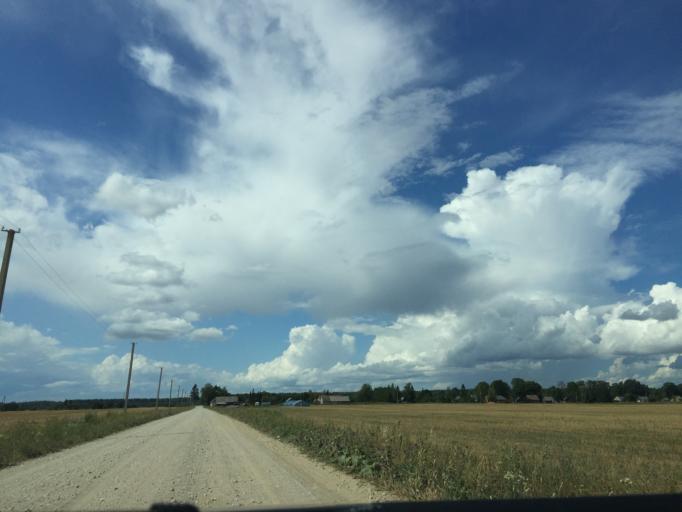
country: LT
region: Siauliu apskritis
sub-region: Joniskis
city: Joniskis
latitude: 56.3379
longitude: 23.6267
